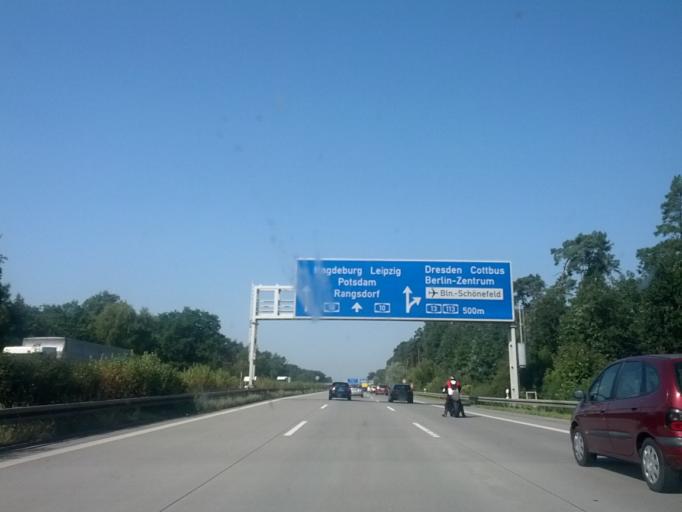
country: DE
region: Brandenburg
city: Schulzendorf
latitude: 52.3199
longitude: 13.5814
